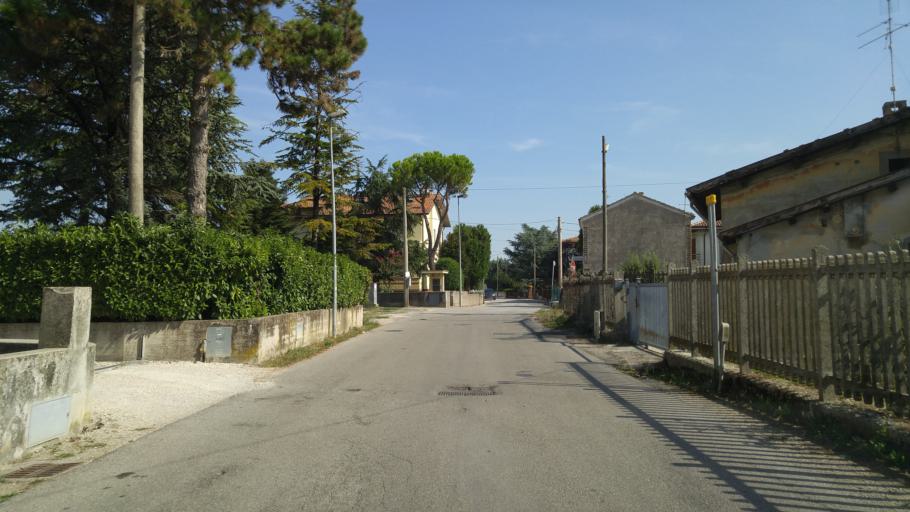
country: IT
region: The Marches
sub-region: Provincia di Pesaro e Urbino
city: Cuccurano
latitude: 43.7993
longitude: 12.9730
